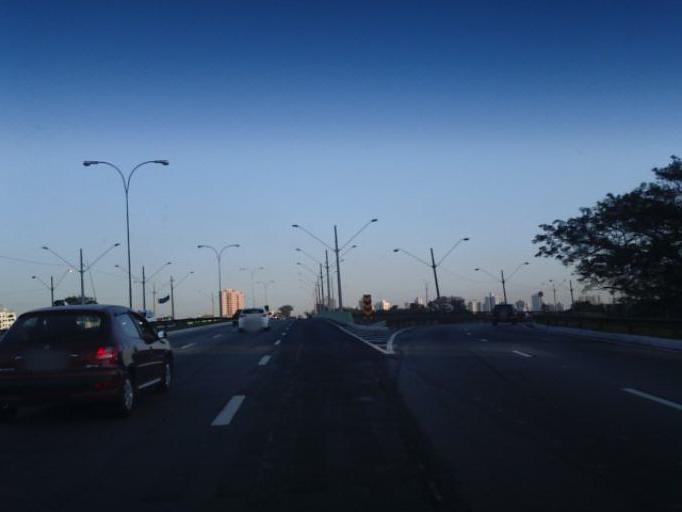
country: BR
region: Sao Paulo
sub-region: Sao Jose Dos Campos
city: Sao Jose dos Campos
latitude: -23.2179
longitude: -45.9011
